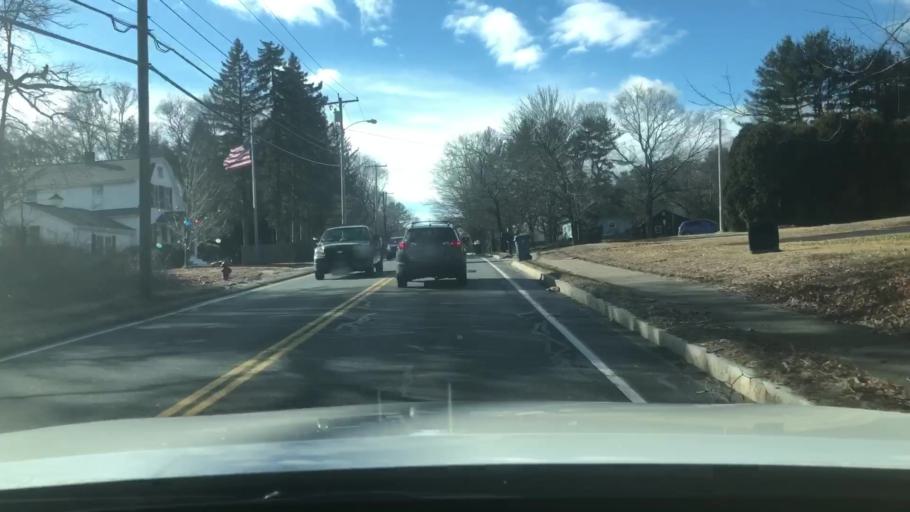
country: US
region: Massachusetts
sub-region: Norfolk County
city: Bellingham
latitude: 42.0651
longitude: -71.4777
